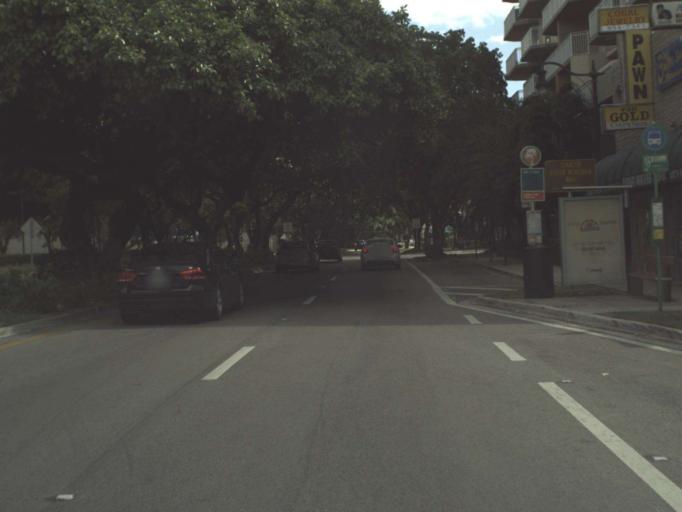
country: US
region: Florida
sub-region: Miami-Dade County
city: Miami
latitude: 25.7508
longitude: -80.2217
